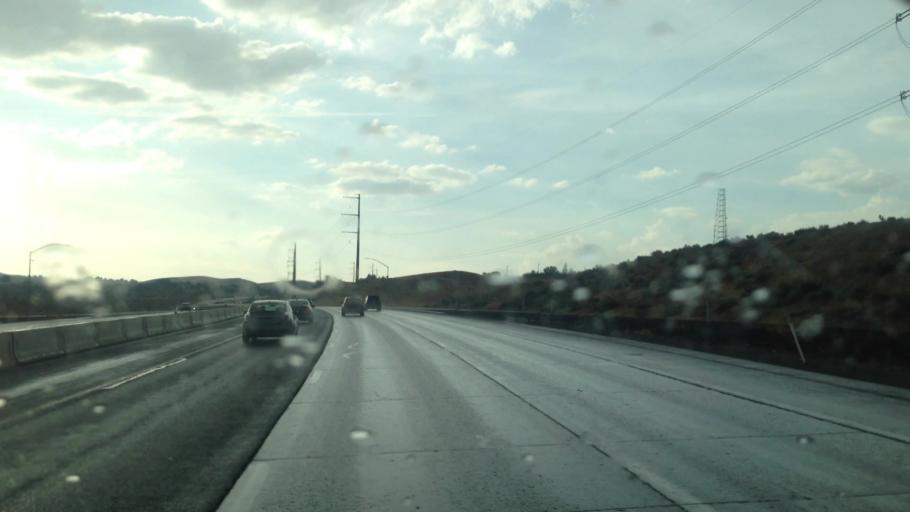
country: US
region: Nevada
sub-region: Washoe County
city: Sun Valley
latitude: 39.5755
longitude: -119.8099
